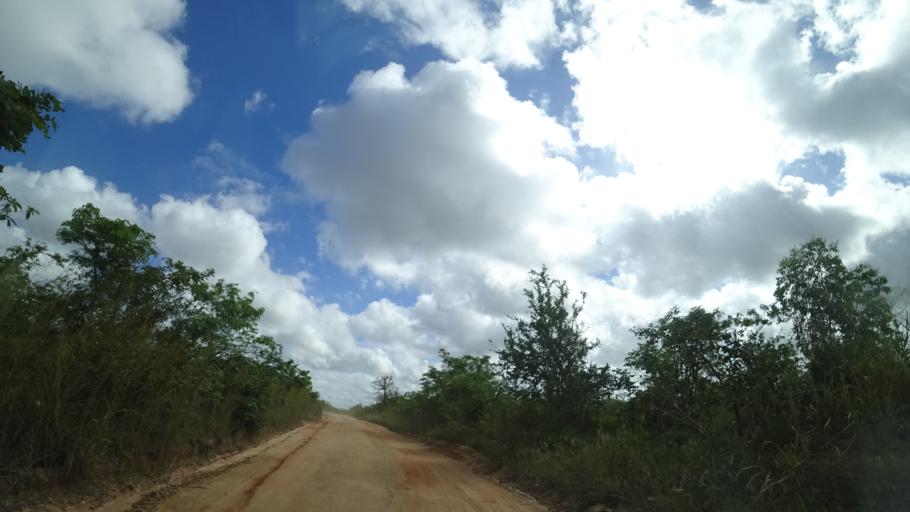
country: MZ
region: Sofala
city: Dondo
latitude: -19.4429
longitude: 34.7157
